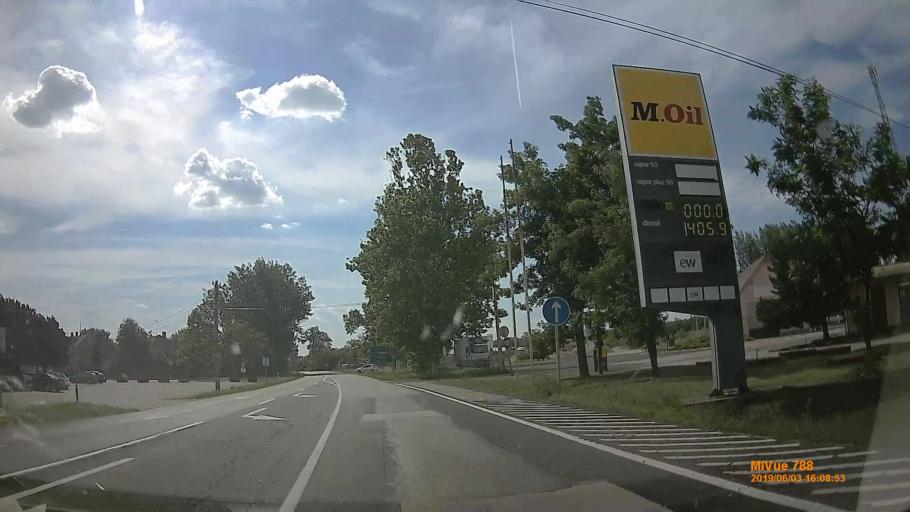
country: HU
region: Bacs-Kiskun
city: Solt
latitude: 46.8191
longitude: 18.9721
